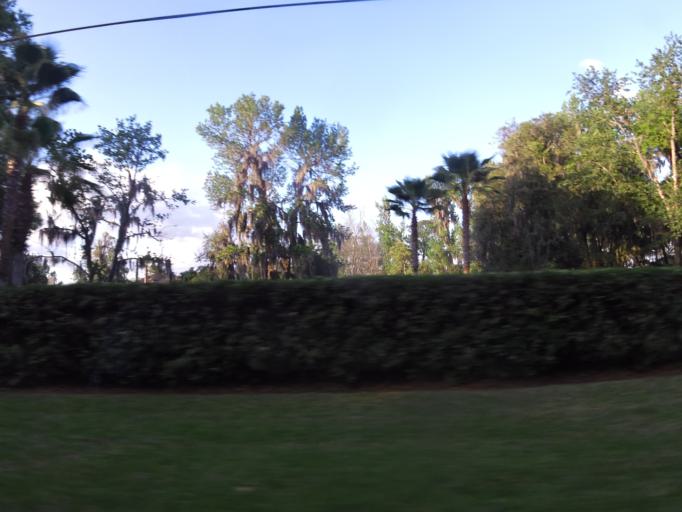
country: US
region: Florida
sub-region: Saint Johns County
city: Fruit Cove
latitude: 30.1240
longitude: -81.5865
